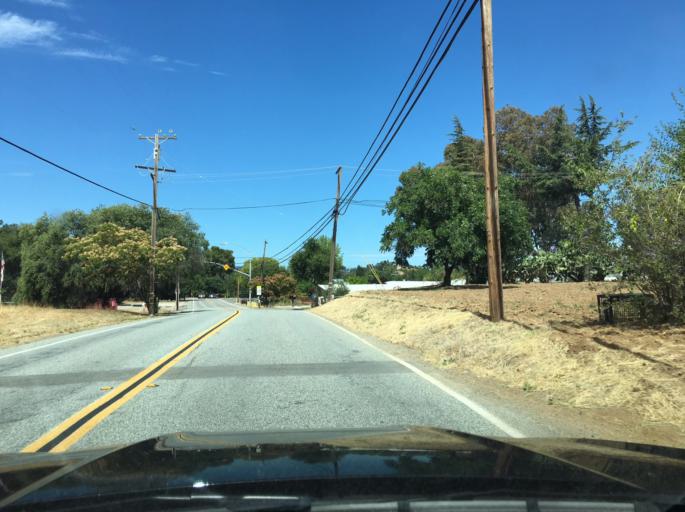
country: US
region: California
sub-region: Santa Clara County
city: Seven Trees
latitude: 37.1998
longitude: -121.8238
